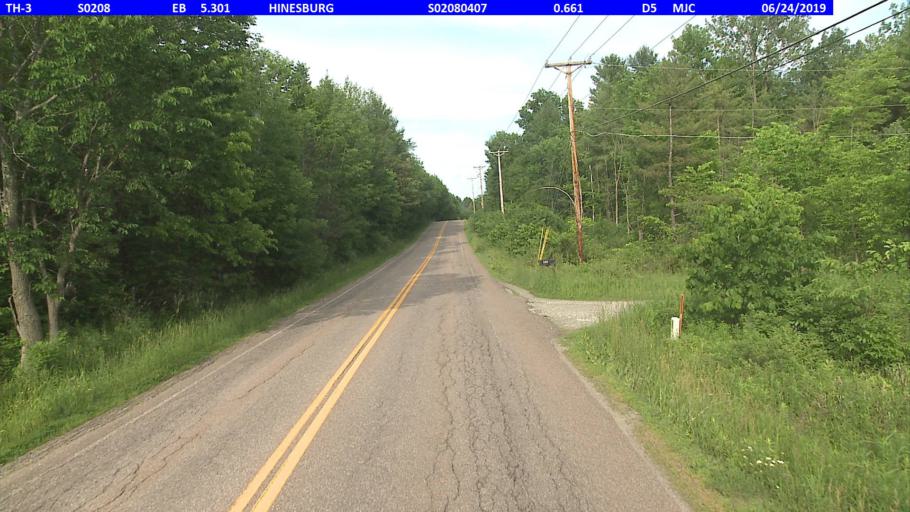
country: US
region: Vermont
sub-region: Chittenden County
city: Hinesburg
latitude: 44.3232
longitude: -73.1429
